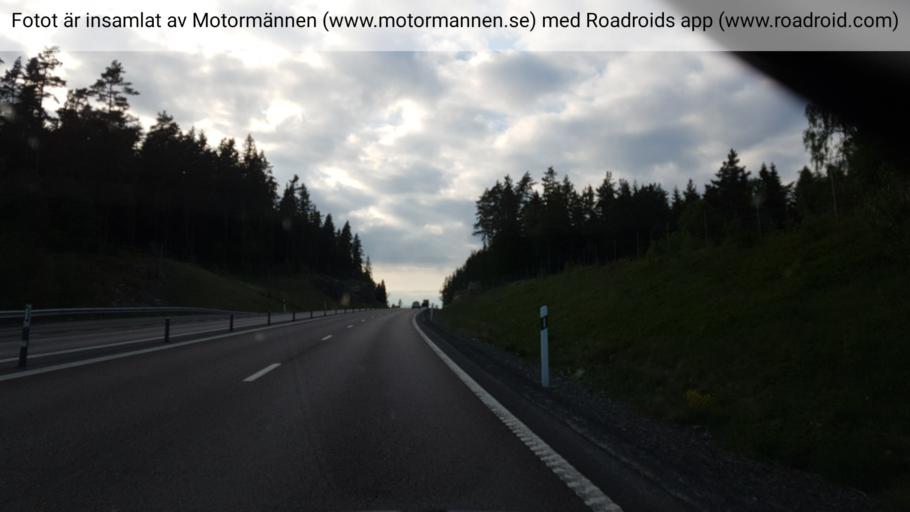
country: SE
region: Joenkoeping
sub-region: Jonkopings Kommun
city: Tenhult
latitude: 57.7235
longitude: 14.3532
